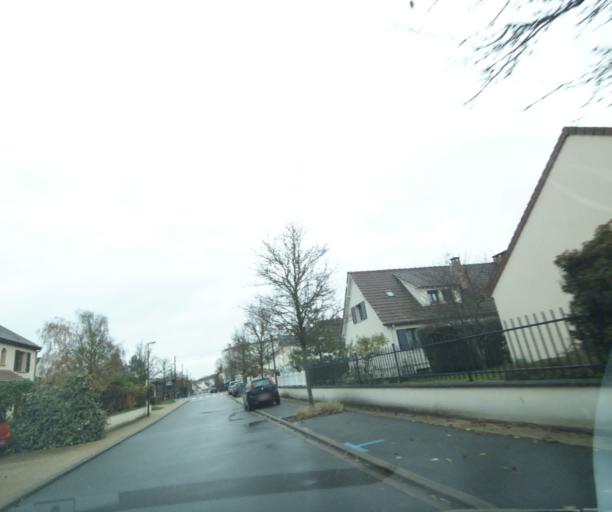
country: FR
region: Ile-de-France
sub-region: Departement de Seine-et-Marne
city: Avon
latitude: 48.4121
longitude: 2.7278
